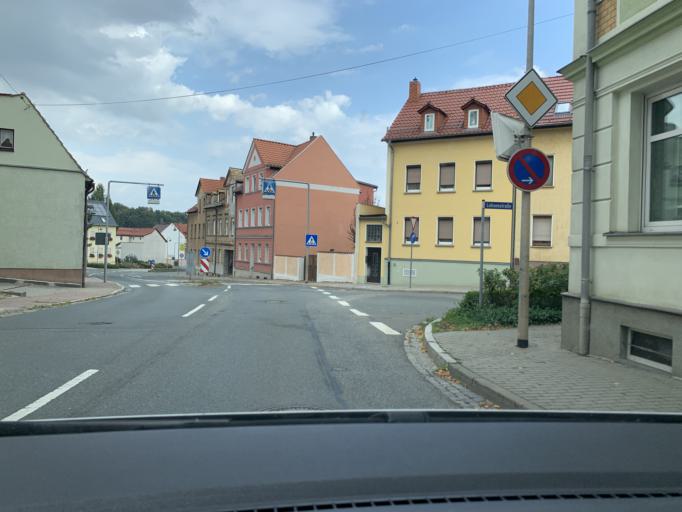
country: DE
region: Thuringia
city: Schmolln
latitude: 50.8924
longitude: 12.3507
